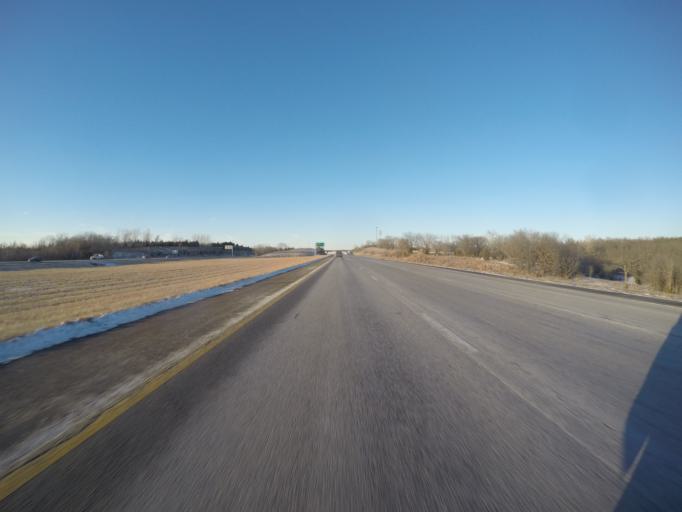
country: US
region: Kansas
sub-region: Wyandotte County
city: Edwardsville
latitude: 39.0288
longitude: -94.7864
